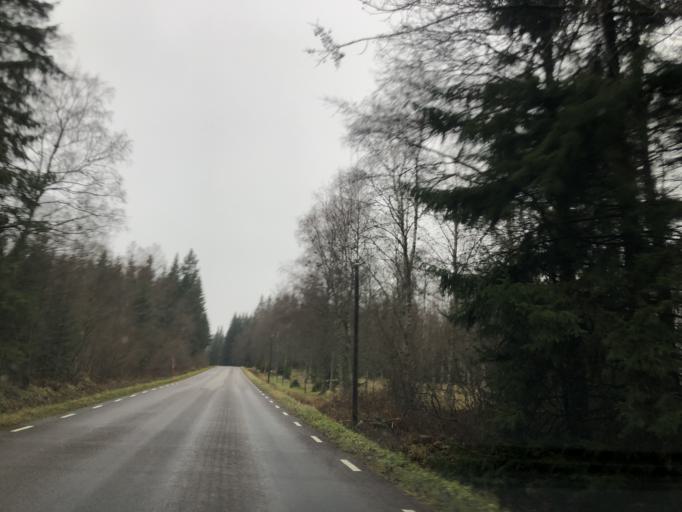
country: SE
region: Vaestra Goetaland
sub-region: Ulricehamns Kommun
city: Ulricehamn
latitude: 57.7613
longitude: 13.4839
